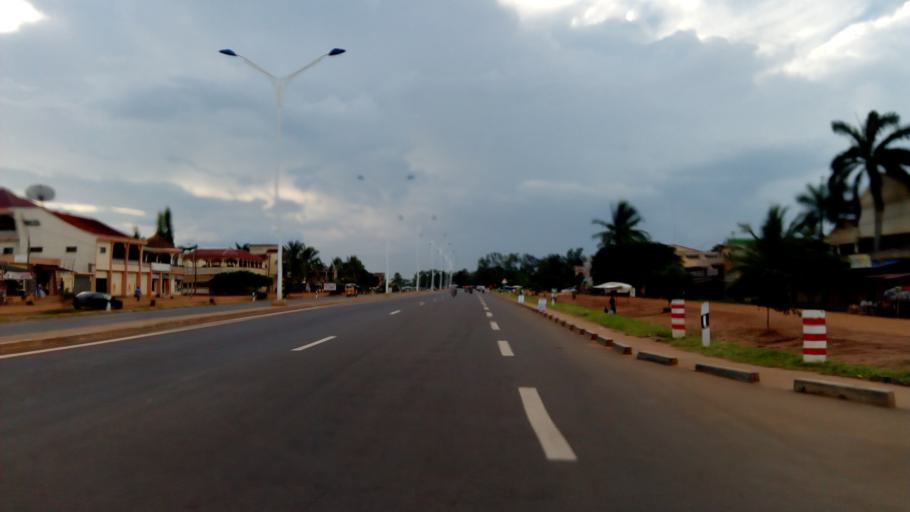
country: TG
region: Maritime
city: Lome
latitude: 6.2438
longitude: 1.1942
